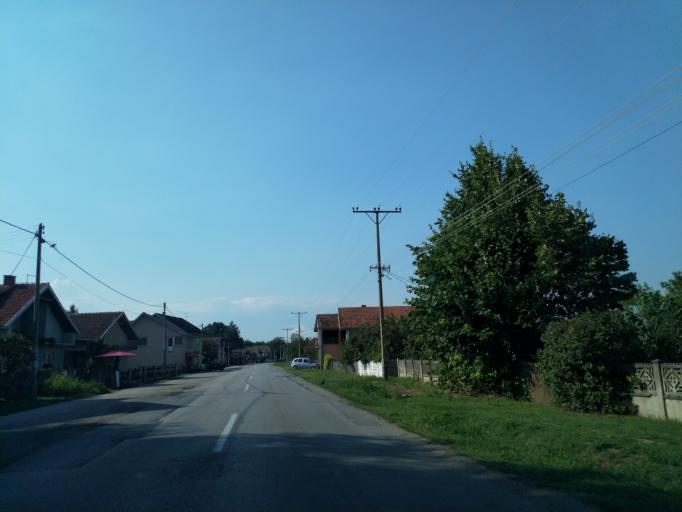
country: RS
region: Central Serbia
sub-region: Rasinski Okrug
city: Cicevac
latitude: 43.7624
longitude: 21.4307
